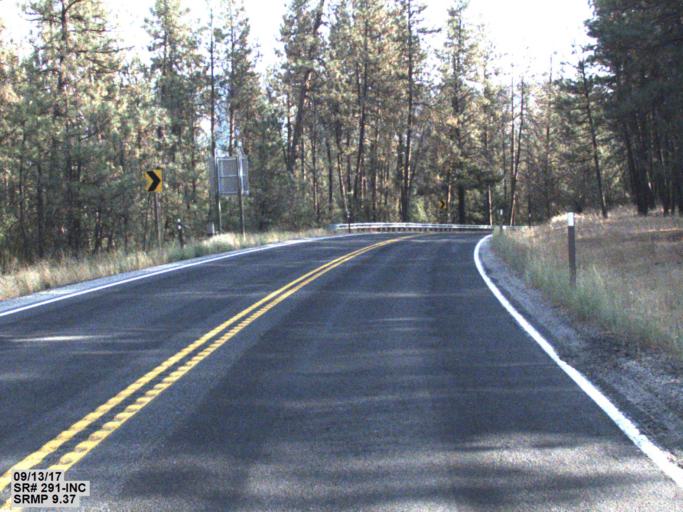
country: US
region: Washington
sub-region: Spokane County
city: Fairwood
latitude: 47.7793
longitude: -117.5433
